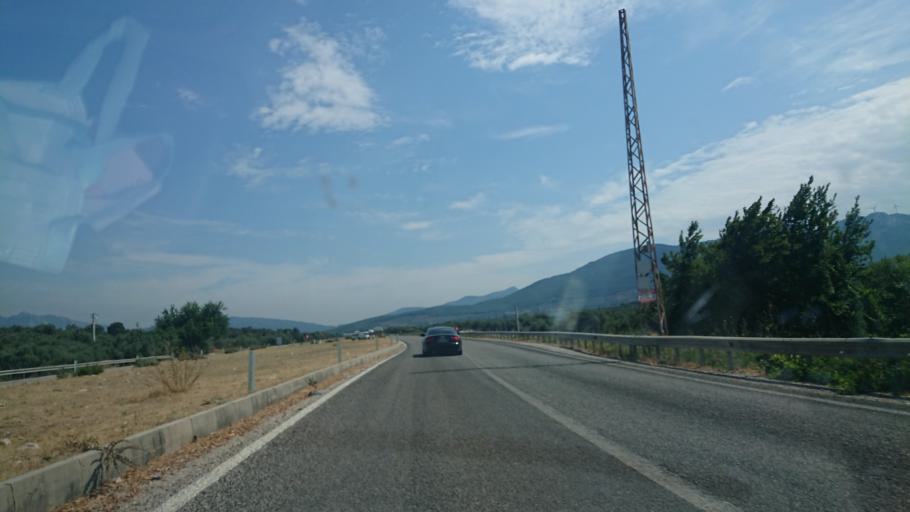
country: TR
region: Izmir
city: Dagkizilca
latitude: 38.2795
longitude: 27.3996
